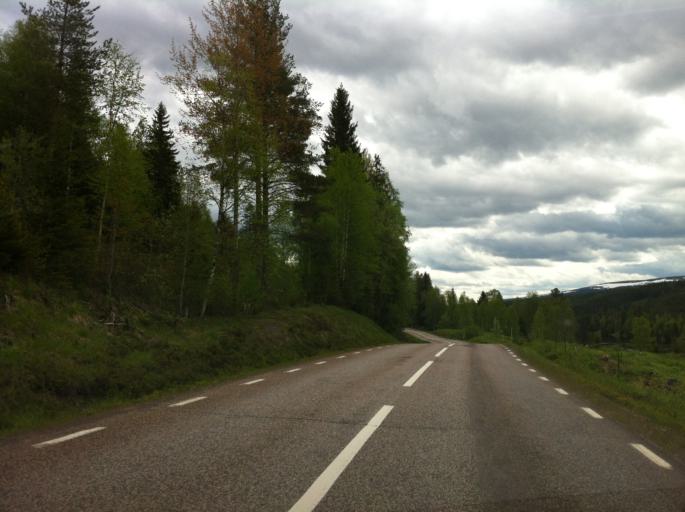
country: SE
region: Dalarna
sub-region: Malung-Saelens kommun
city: Malung
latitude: 61.2452
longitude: 13.2123
